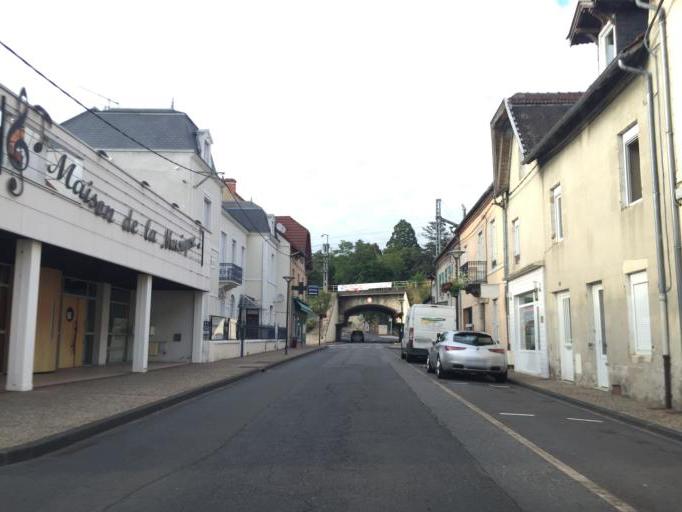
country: FR
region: Auvergne
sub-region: Departement de l'Allier
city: Saint-Germain-des-Fosses
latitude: 46.2063
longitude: 3.4329
